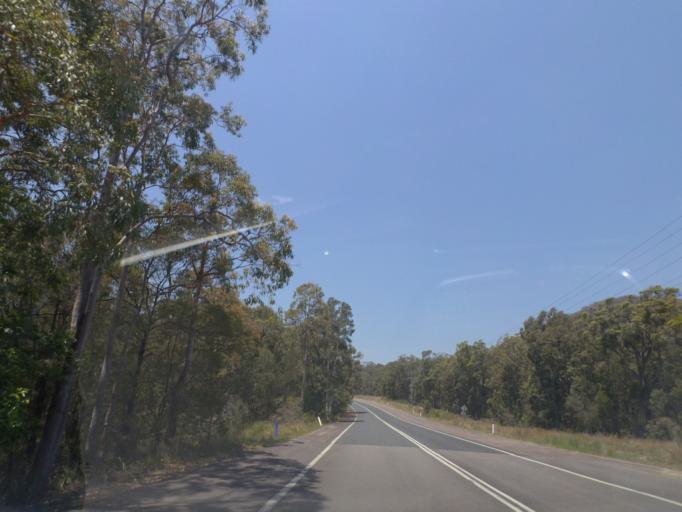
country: AU
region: New South Wales
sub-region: Port Stephens Shire
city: Port Stephens
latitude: -32.6375
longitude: 152.0203
